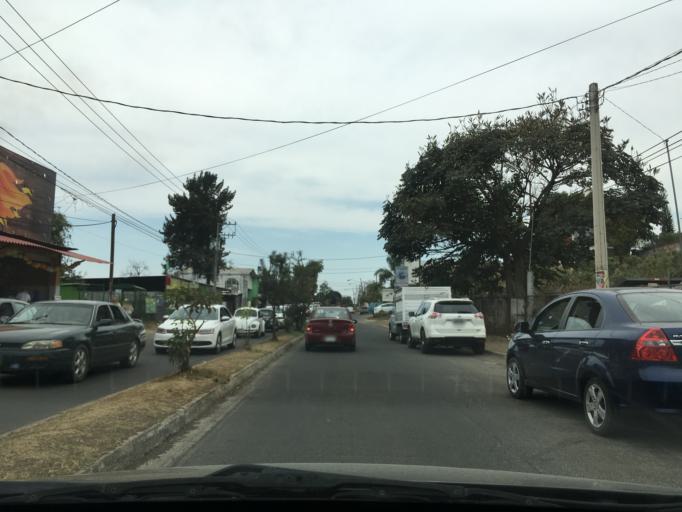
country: MX
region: Michoacan
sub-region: Uruapan
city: Uruapan
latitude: 19.3897
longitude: -102.0702
